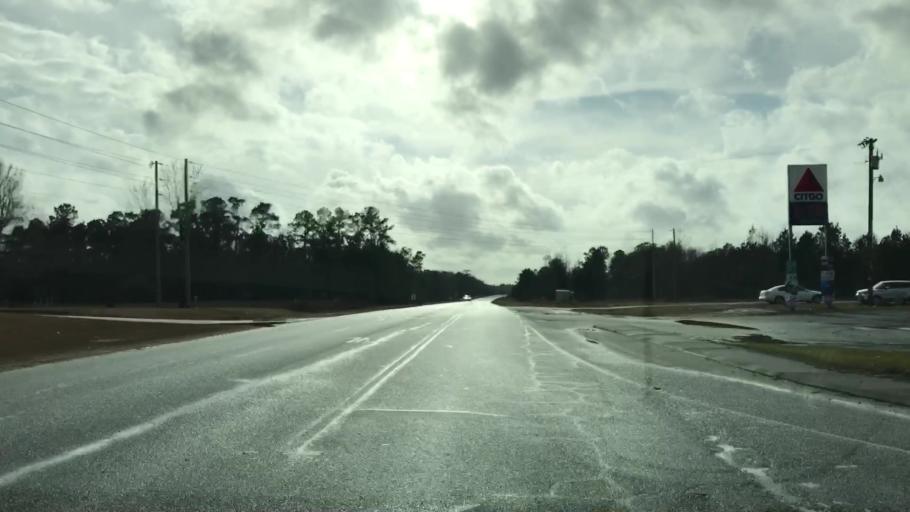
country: US
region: South Carolina
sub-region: Williamsburg County
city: Andrews
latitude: 33.4941
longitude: -79.5418
